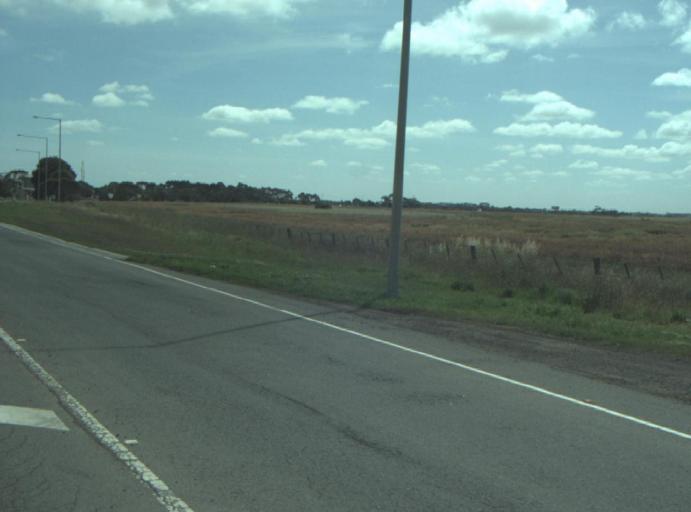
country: AU
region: Victoria
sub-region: Greater Geelong
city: Lara
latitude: -38.0338
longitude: 144.4316
